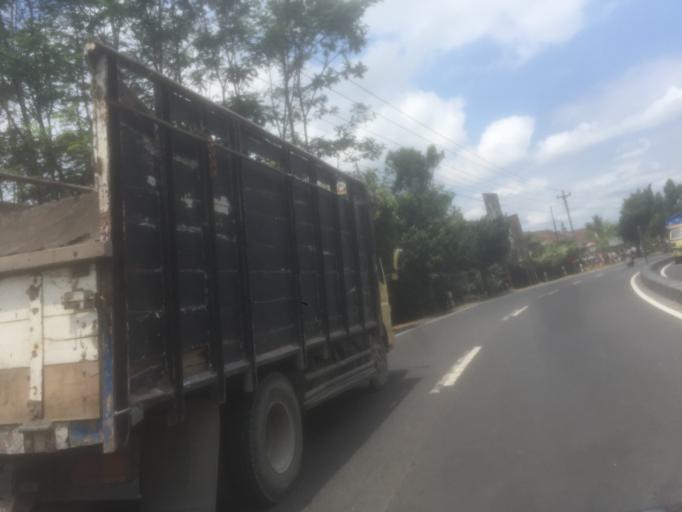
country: ID
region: Central Java
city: Muntilan
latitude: -7.6293
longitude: 110.3214
